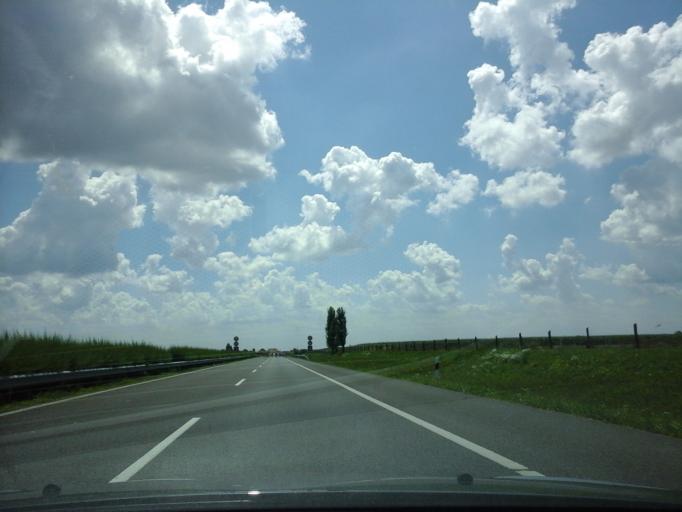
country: HU
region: Hajdu-Bihar
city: Ebes
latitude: 47.5068
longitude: 21.5481
